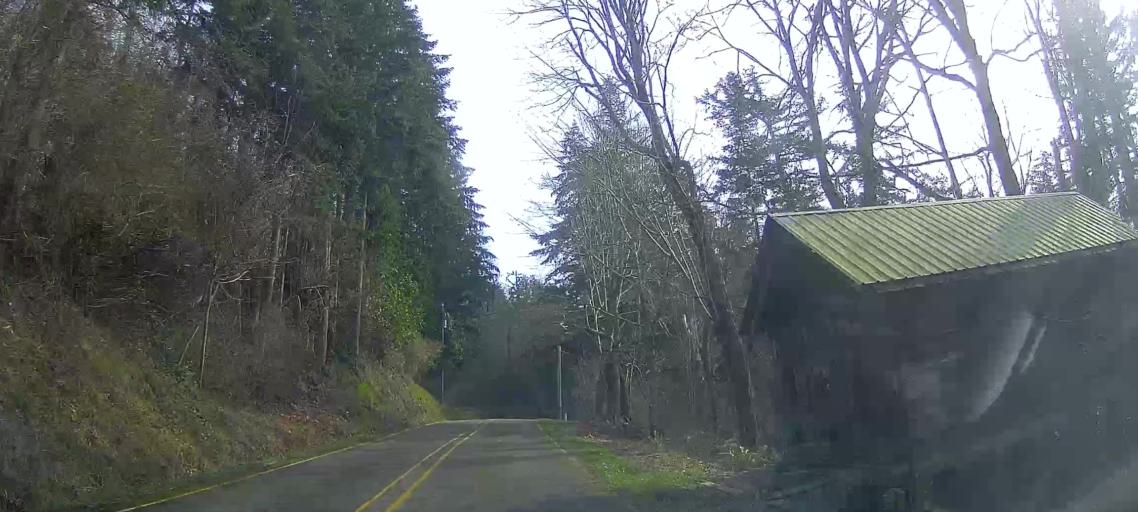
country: US
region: Washington
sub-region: Island County
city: Langley
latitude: 48.0633
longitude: -122.3825
